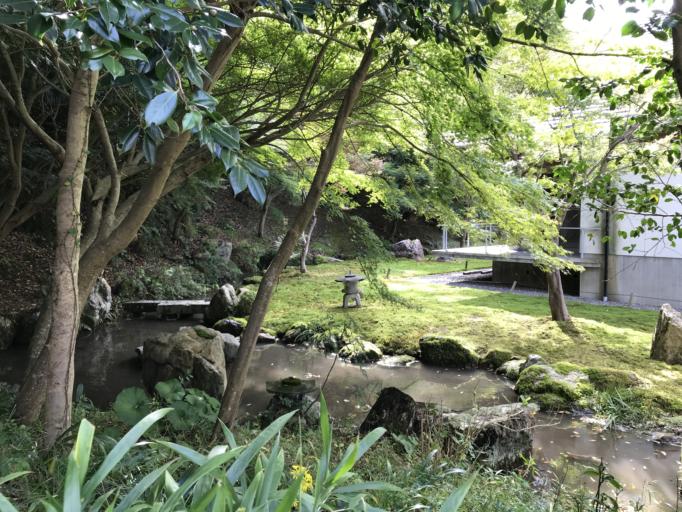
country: JP
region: Fukui
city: Obama
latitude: 35.4898
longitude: 135.7352
